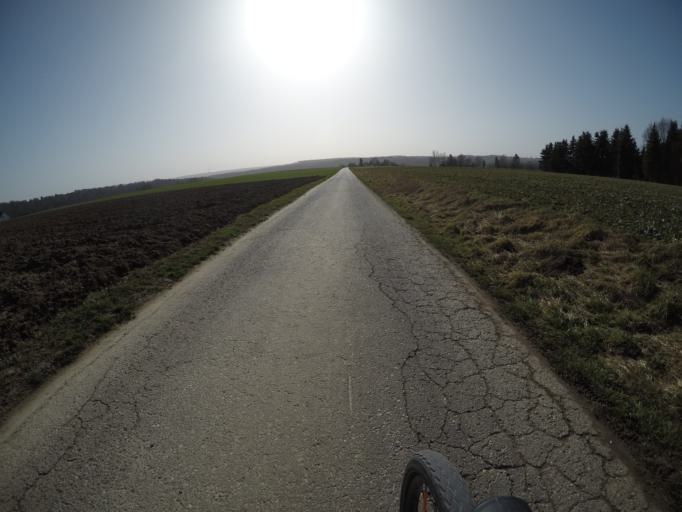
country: DE
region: Baden-Wuerttemberg
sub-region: Regierungsbezirk Stuttgart
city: Schonaich
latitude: 48.6612
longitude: 9.0757
